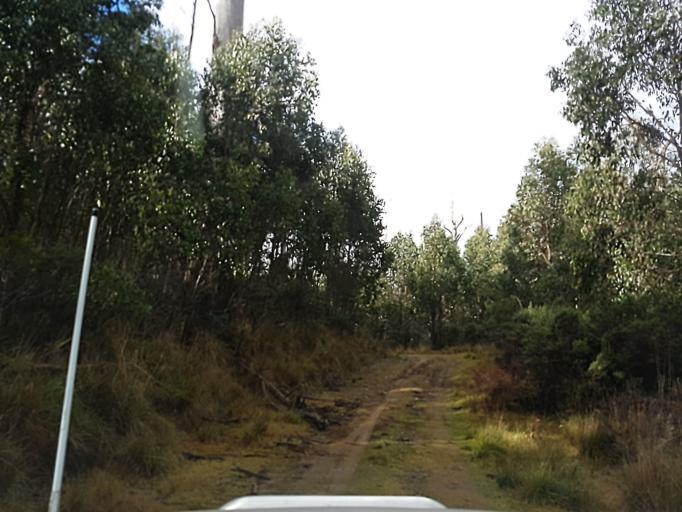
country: AU
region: Victoria
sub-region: Yarra Ranges
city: Millgrove
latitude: -37.5349
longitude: 145.8066
